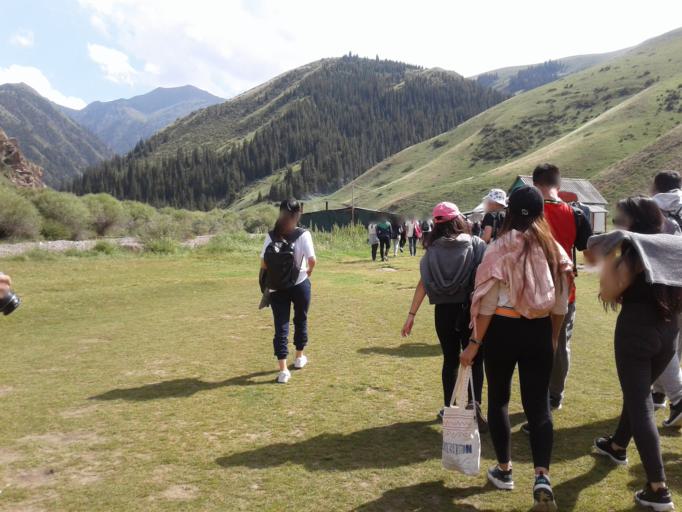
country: KG
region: Naryn
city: Naryn
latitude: 41.4600
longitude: 76.4537
